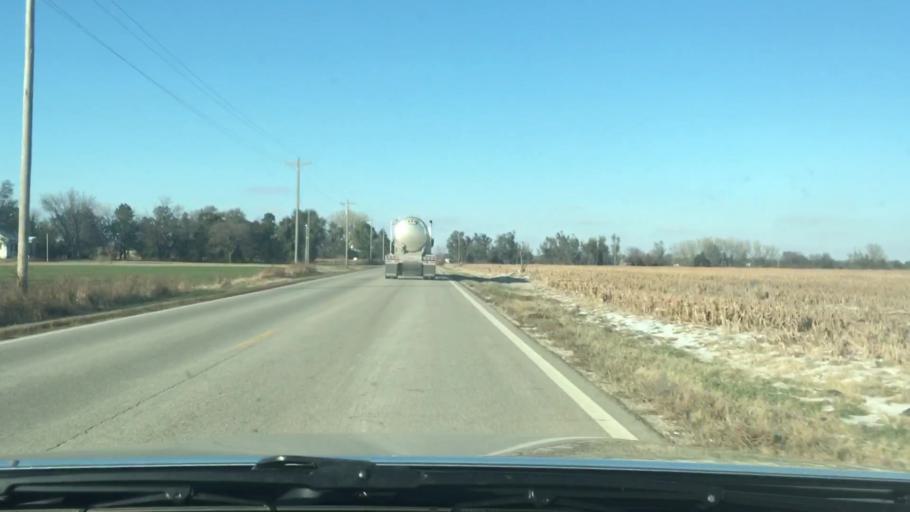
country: US
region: Kansas
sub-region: Rice County
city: Sterling
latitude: 38.1884
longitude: -98.2068
